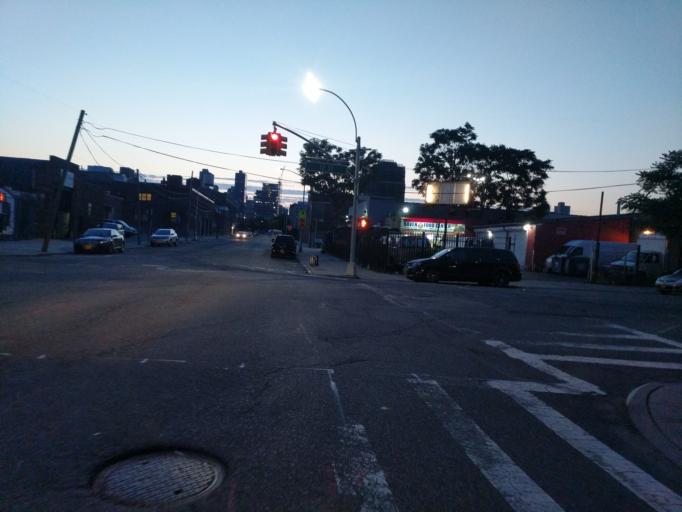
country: US
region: New York
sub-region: Queens County
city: Long Island City
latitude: 40.7625
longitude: -73.9378
